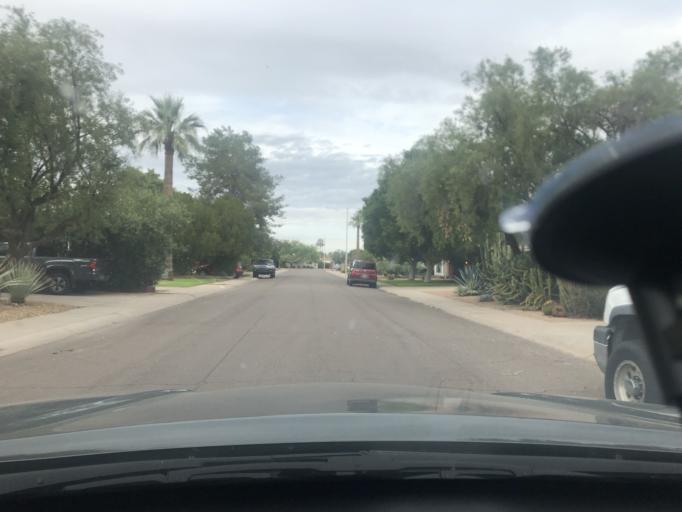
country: US
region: Arizona
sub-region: Maricopa County
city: Scottsdale
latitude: 33.4884
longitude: -111.9030
